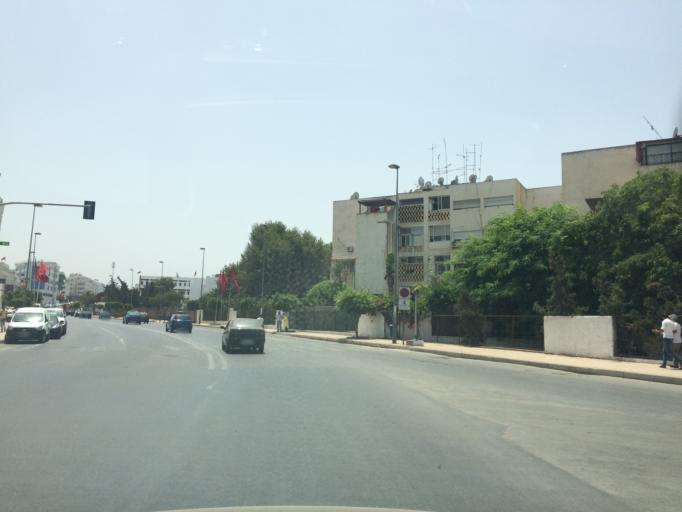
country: MA
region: Rabat-Sale-Zemmour-Zaer
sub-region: Rabat
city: Rabat
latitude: 34.0019
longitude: -6.8515
